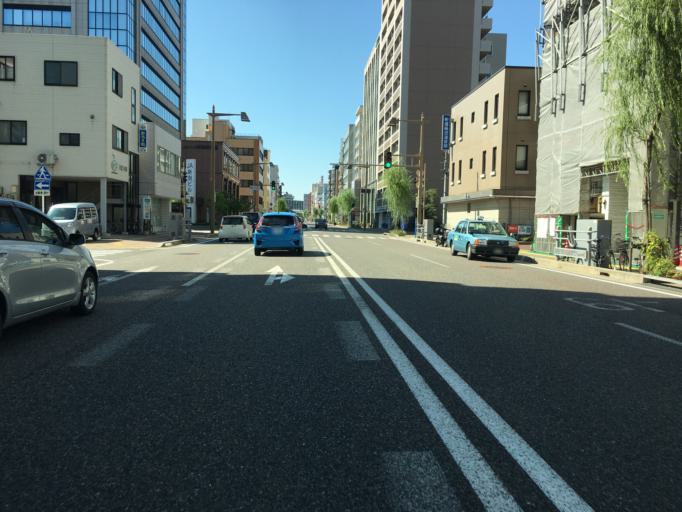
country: JP
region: Niigata
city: Niigata-shi
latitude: 37.9206
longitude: 139.0400
